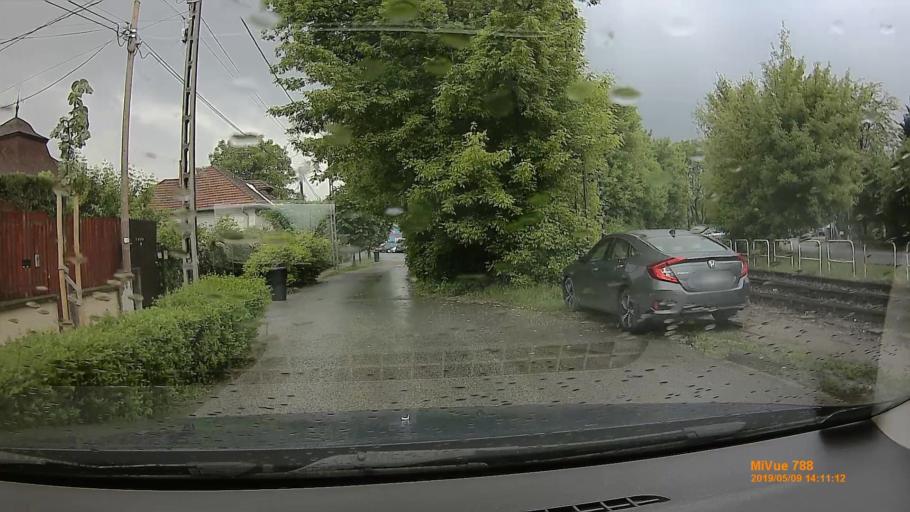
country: HU
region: Budapest
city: Budapest XVI. keruelet
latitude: 47.5092
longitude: 19.1730
